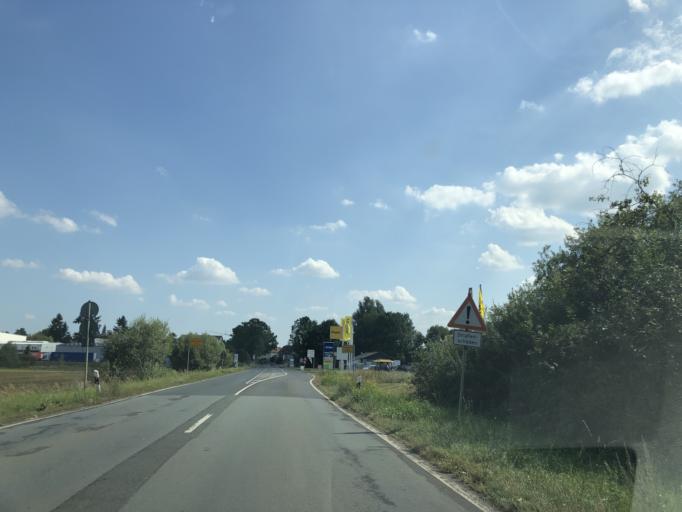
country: DE
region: Hesse
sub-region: Regierungsbezirk Giessen
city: Kirchhain
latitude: 50.8292
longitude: 8.9086
